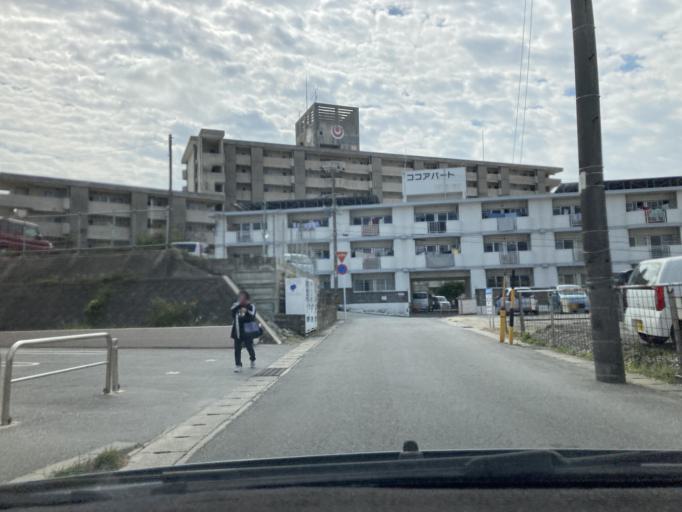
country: JP
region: Okinawa
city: Tomigusuku
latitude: 26.1986
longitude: 127.6936
